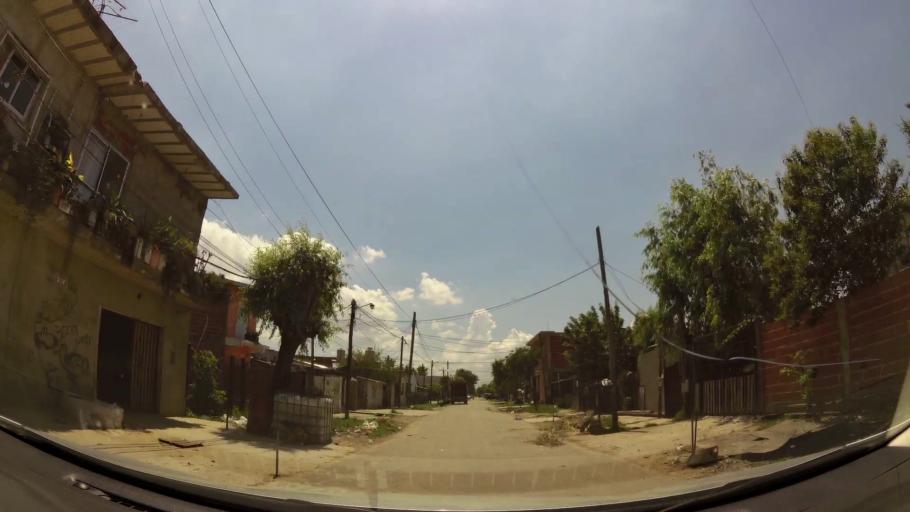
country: AR
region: Buenos Aires
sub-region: Partido de Tigre
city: Tigre
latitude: -34.4552
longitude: -58.5989
